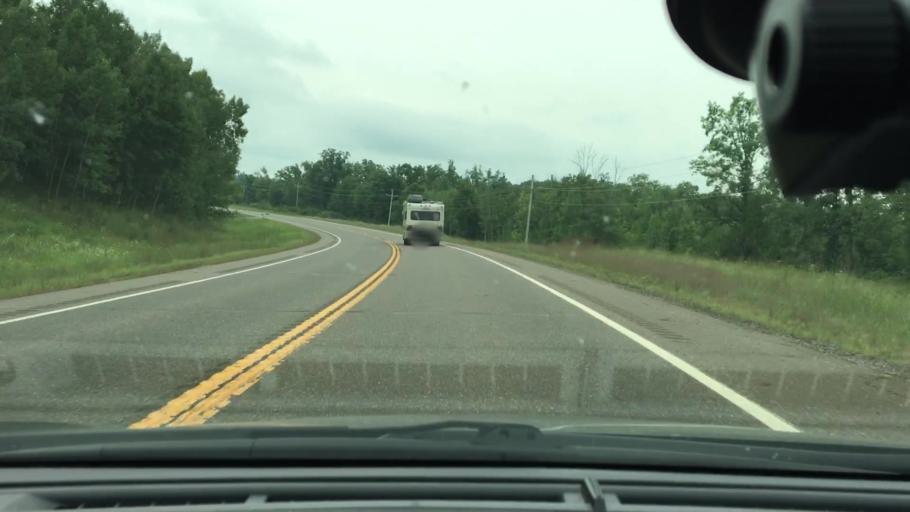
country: US
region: Minnesota
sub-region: Crow Wing County
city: Crosby
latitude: 46.5088
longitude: -93.9602
